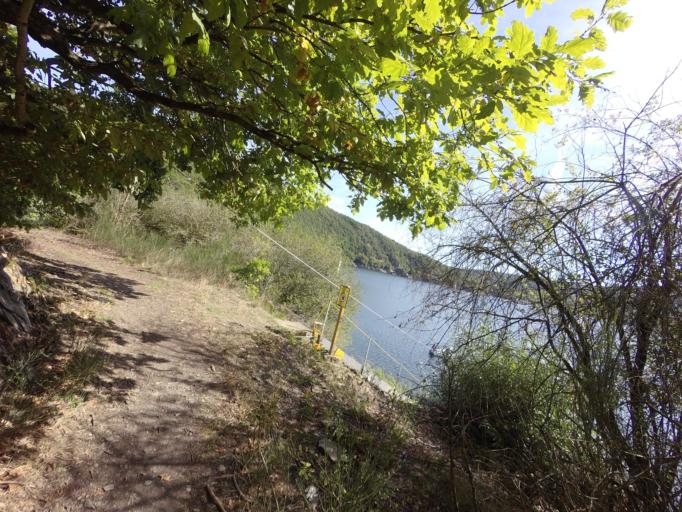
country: DE
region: North Rhine-Westphalia
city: Heimbach
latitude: 50.6332
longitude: 6.3907
